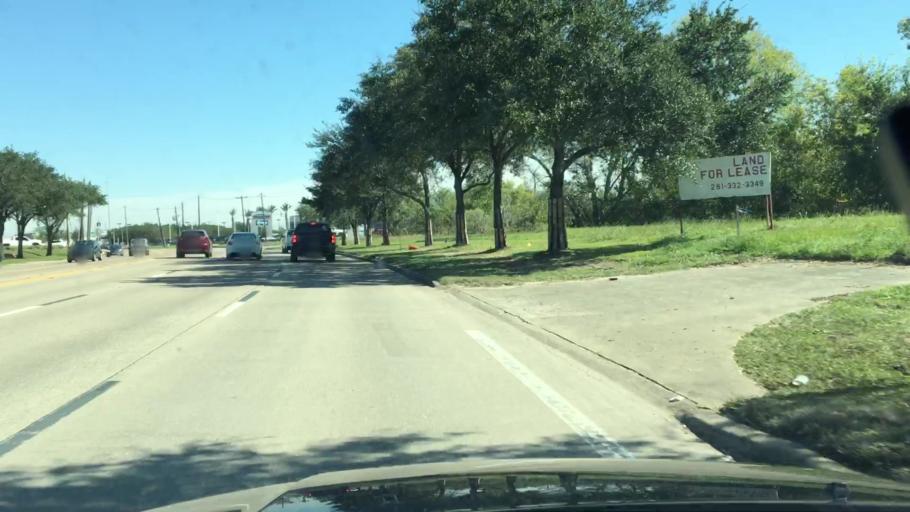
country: US
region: Texas
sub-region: Harris County
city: Webster
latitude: 29.5249
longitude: -95.1369
